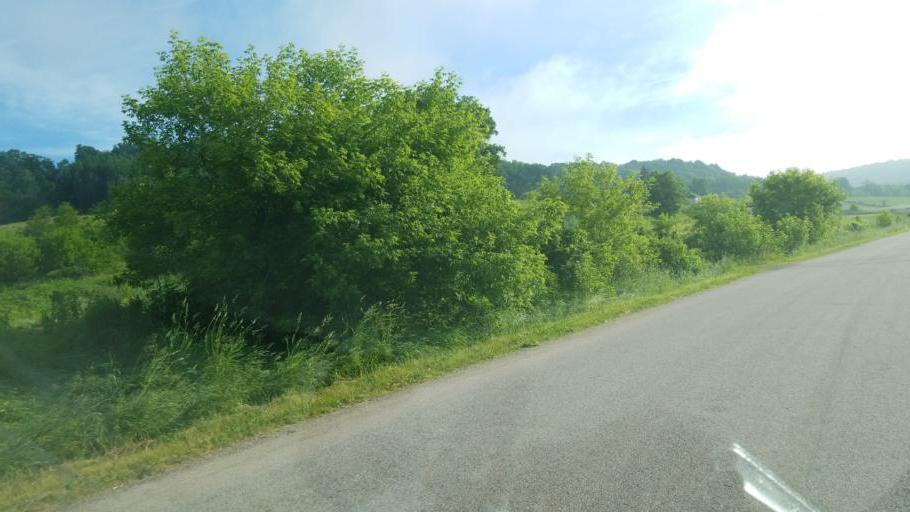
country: US
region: Wisconsin
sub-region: Vernon County
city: Hillsboro
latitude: 43.6075
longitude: -90.3682
